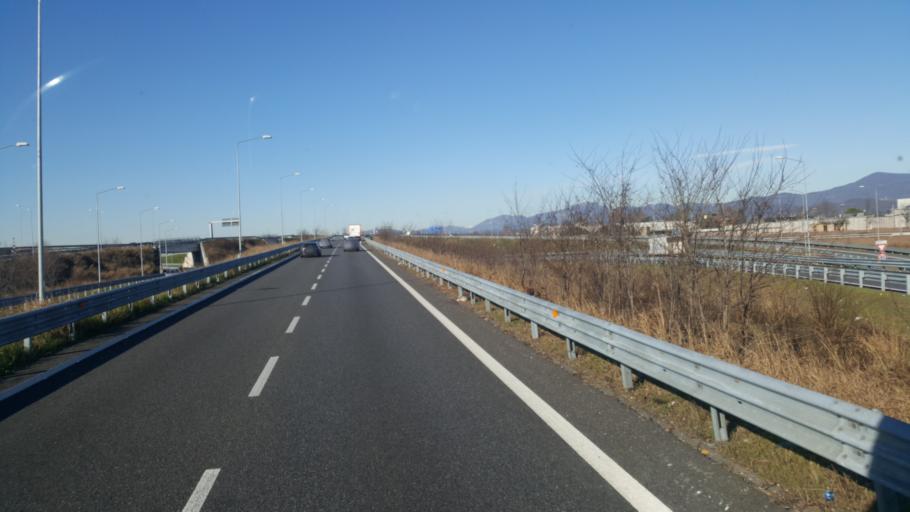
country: IT
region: Lombardy
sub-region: Provincia di Brescia
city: Castegnato
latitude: 45.5464
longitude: 10.1360
